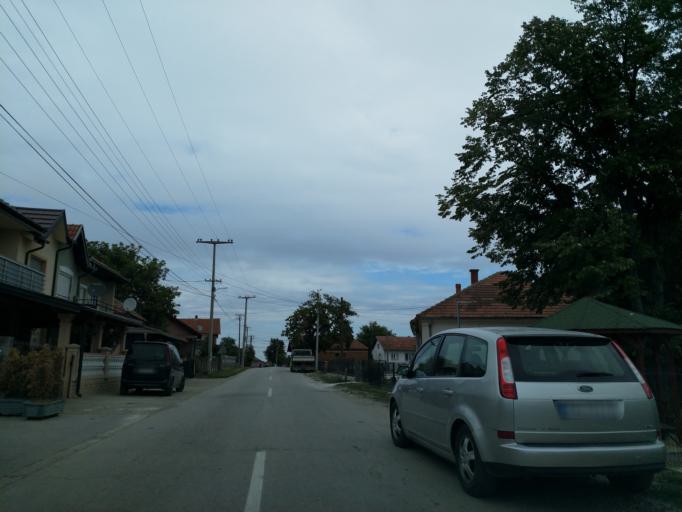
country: RS
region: Central Serbia
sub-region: Pomoravski Okrug
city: Cuprija
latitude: 43.8698
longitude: 21.3221
